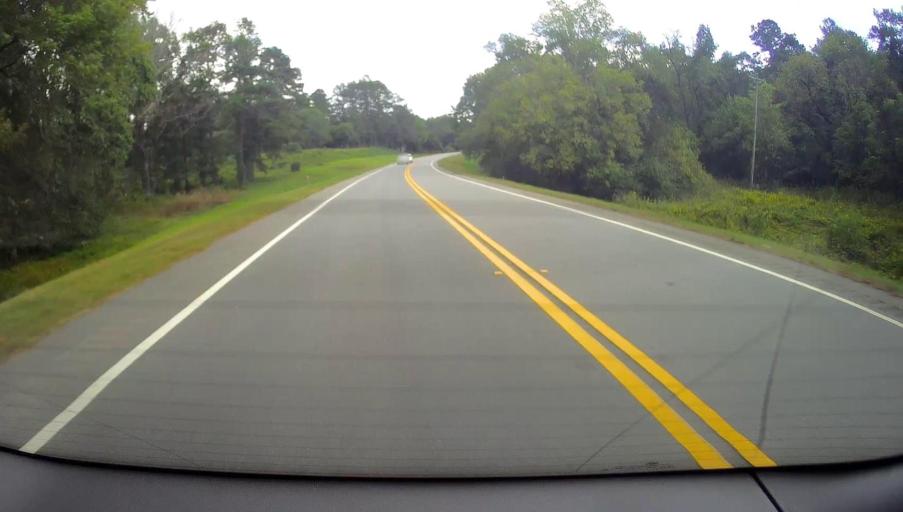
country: US
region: Georgia
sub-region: Baldwin County
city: Milledgeville
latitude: 33.0750
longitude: -83.3331
